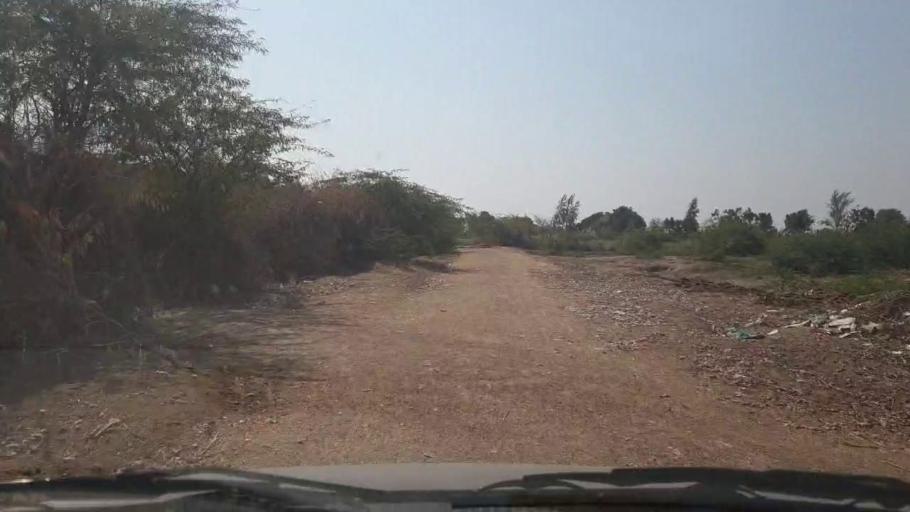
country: PK
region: Sindh
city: Samaro
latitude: 25.2535
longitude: 69.3241
